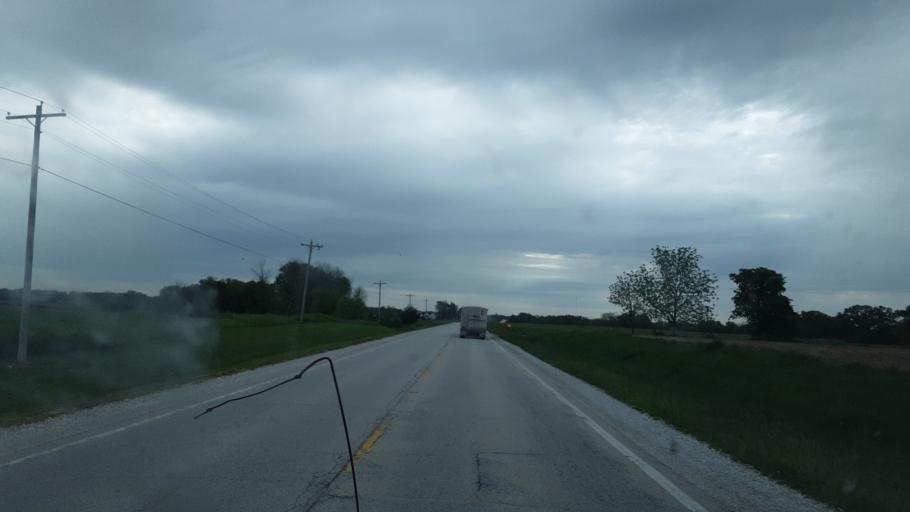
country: US
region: Illinois
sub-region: Fulton County
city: Lewistown
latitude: 40.3419
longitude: -90.2451
